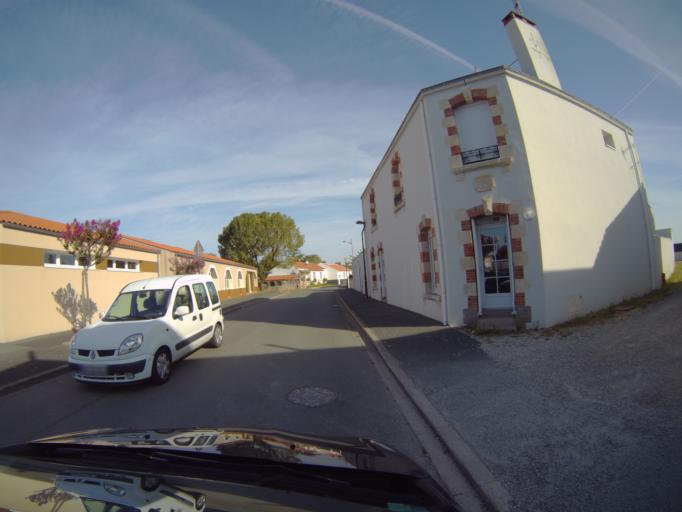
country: FR
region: Pays de la Loire
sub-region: Departement de la Vendee
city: Nieul-le-Dolent
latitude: 46.5756
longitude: -1.5105
